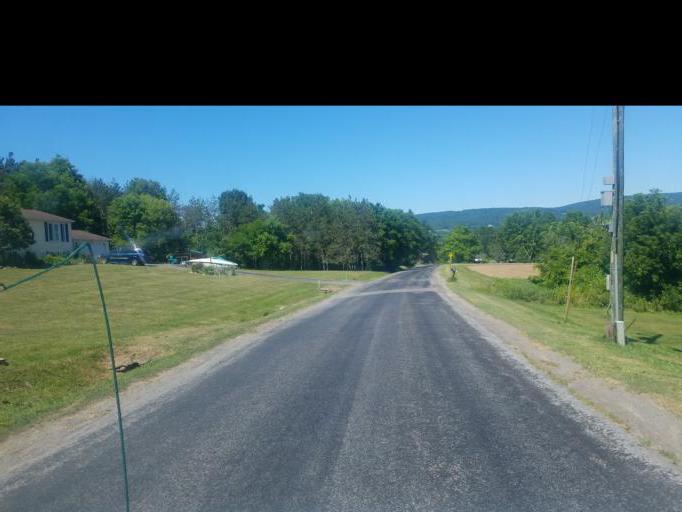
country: US
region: New York
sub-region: Ontario County
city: Naples
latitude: 42.7212
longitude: -77.3161
